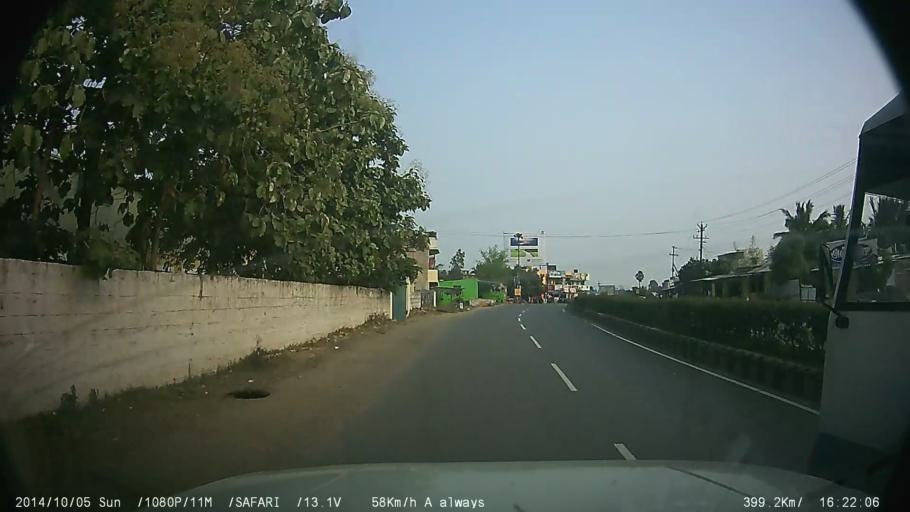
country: IN
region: Tamil Nadu
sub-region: Kancheepuram
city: Vengavasal
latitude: 12.8385
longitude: 80.1546
